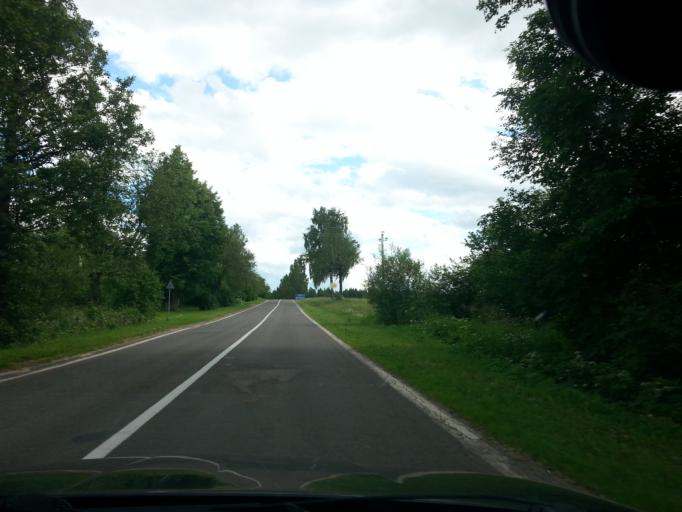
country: BY
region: Minsk
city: Svir
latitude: 54.8979
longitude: 26.3868
